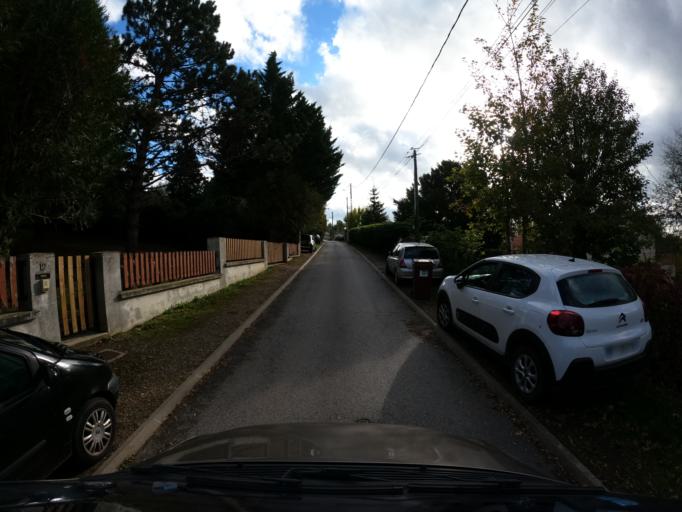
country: FR
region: Ile-de-France
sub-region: Departement de Seine-et-Marne
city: Chalifert
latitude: 48.8898
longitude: 2.7716
